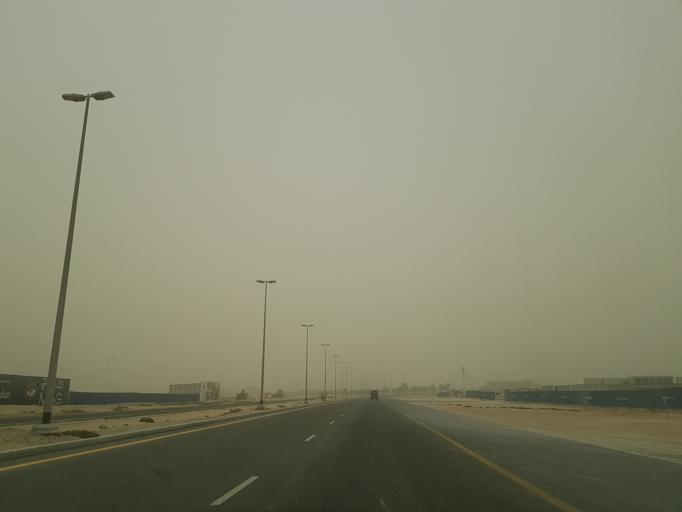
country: AE
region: Dubai
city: Dubai
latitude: 25.1466
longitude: 55.2868
